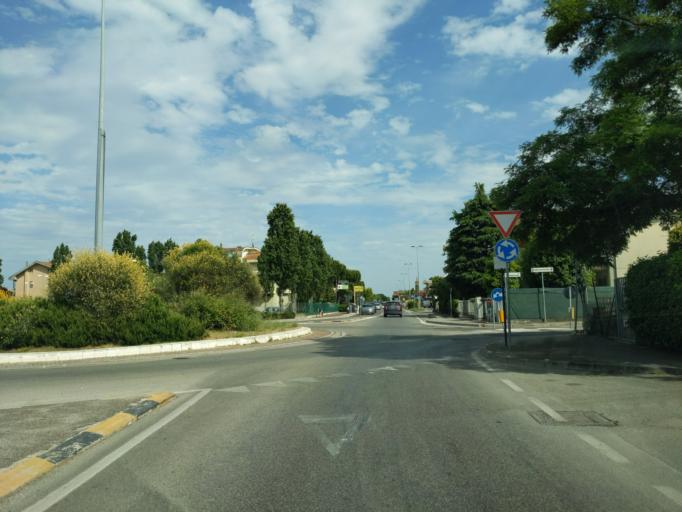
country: IT
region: Emilia-Romagna
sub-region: Provincia di Rimini
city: Rimini
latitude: 44.0452
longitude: 12.5846
